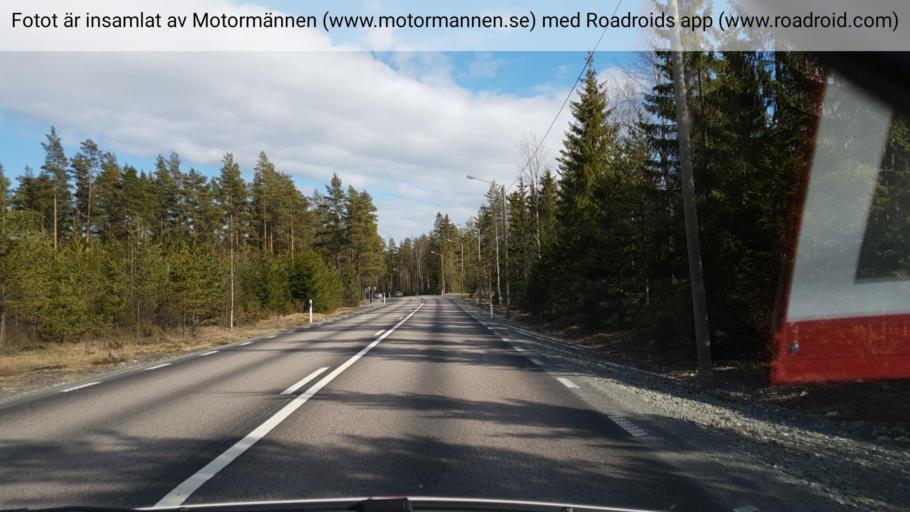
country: SE
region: Vaesternorrland
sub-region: Solleftea Kommun
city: Solleftea
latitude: 63.1499
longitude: 17.3400
